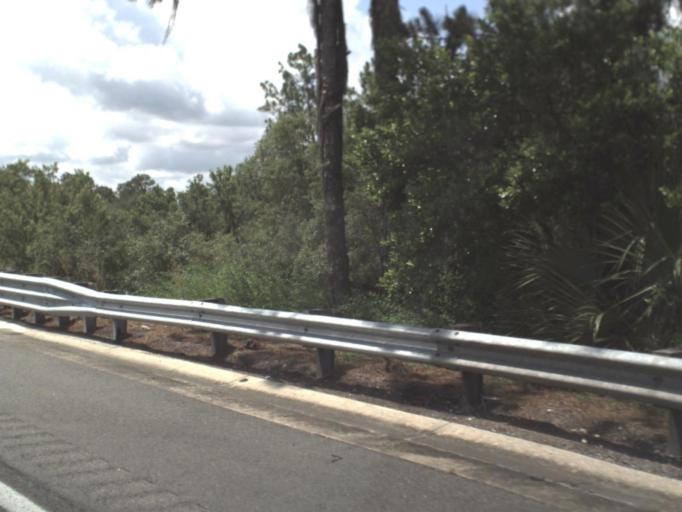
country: US
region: Florida
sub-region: Suwannee County
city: Wellborn
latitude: 30.3469
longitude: -82.8334
